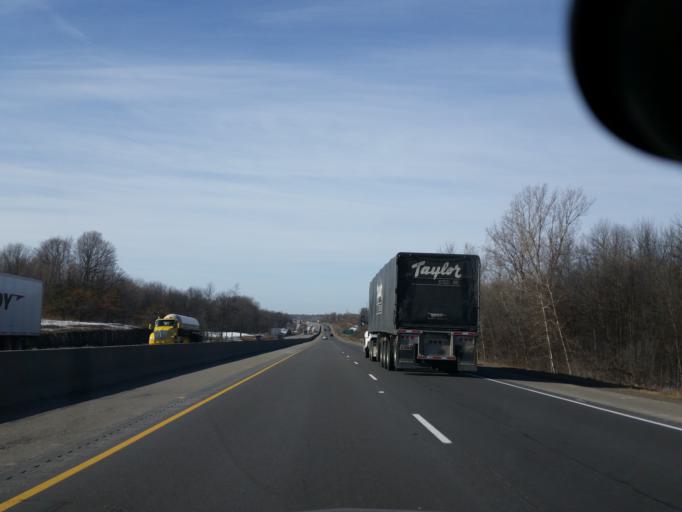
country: CA
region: Ontario
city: Brockville
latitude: 44.6226
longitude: -75.6684
